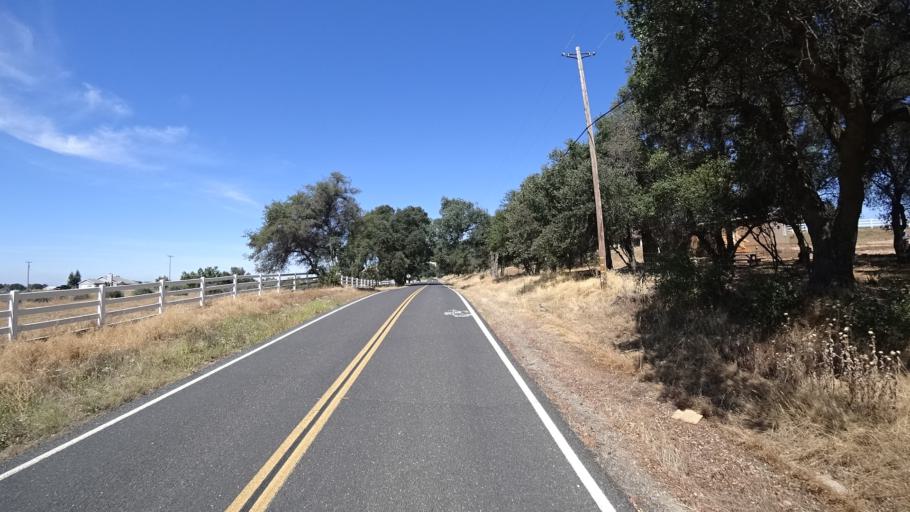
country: US
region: California
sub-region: Calaveras County
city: Rancho Calaveras
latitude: 38.1486
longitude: -120.9186
